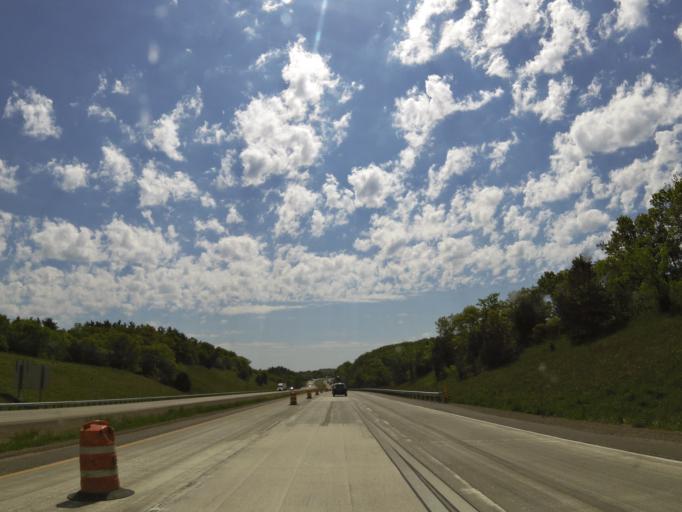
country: US
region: Wisconsin
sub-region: Eau Claire County
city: Eau Claire
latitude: 44.7768
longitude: -91.5282
